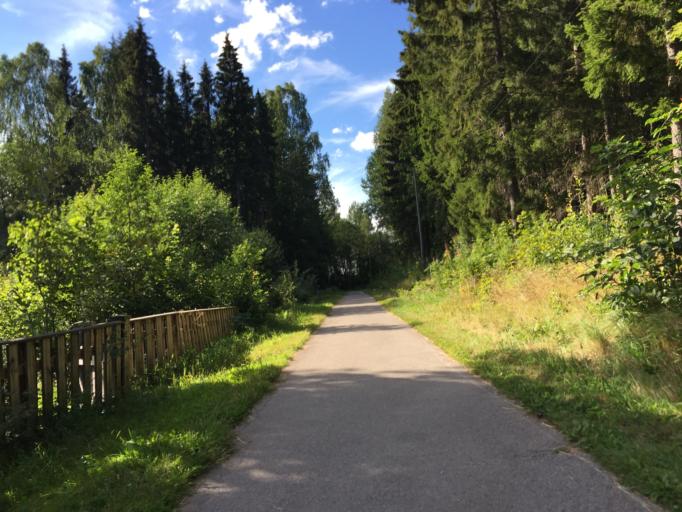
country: NO
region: Hedmark
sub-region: Kongsvinger
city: Kongsvinger
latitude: 60.1965
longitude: 11.9912
